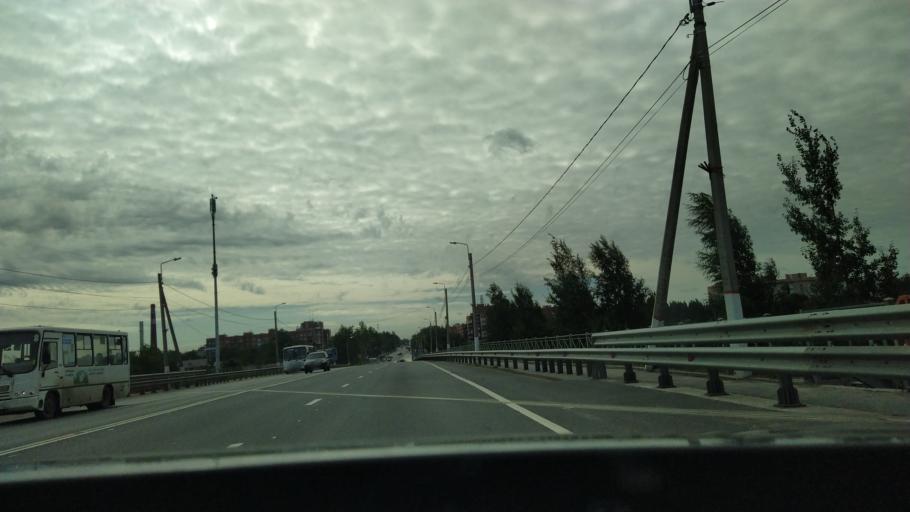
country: RU
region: Leningrad
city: Tosno
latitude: 59.5496
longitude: 30.8593
